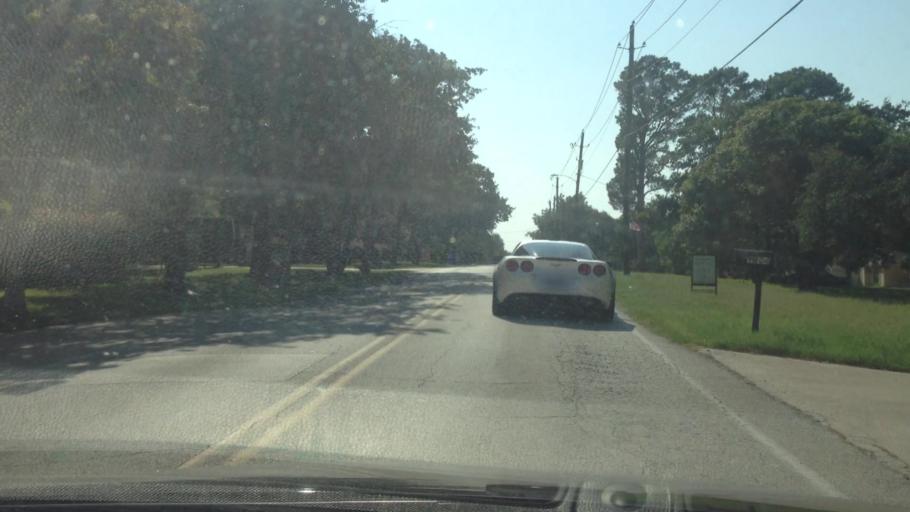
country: US
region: Texas
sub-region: Tarrant County
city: Colleyville
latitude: 32.9004
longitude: -97.1481
